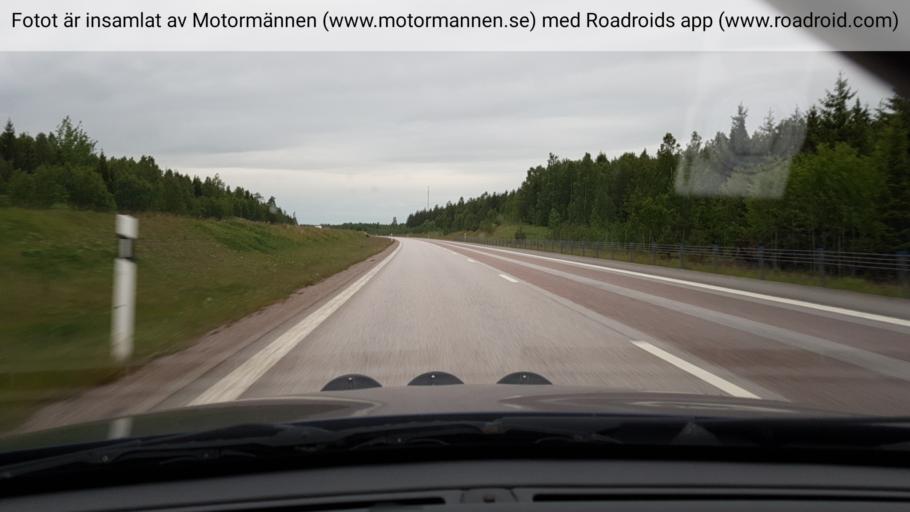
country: SE
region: Uppsala
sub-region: Osthammars Kommun
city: Bjorklinge
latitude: 60.0362
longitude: 17.6296
